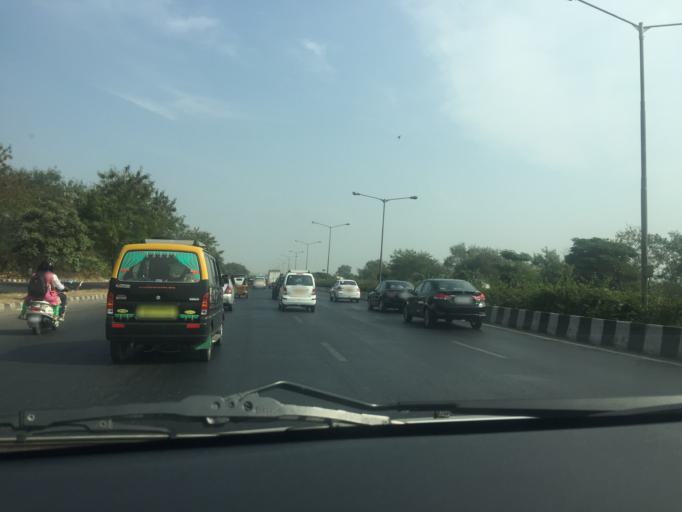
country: IN
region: Maharashtra
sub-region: Mumbai Suburban
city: Powai
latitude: 19.1383
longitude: 72.9465
